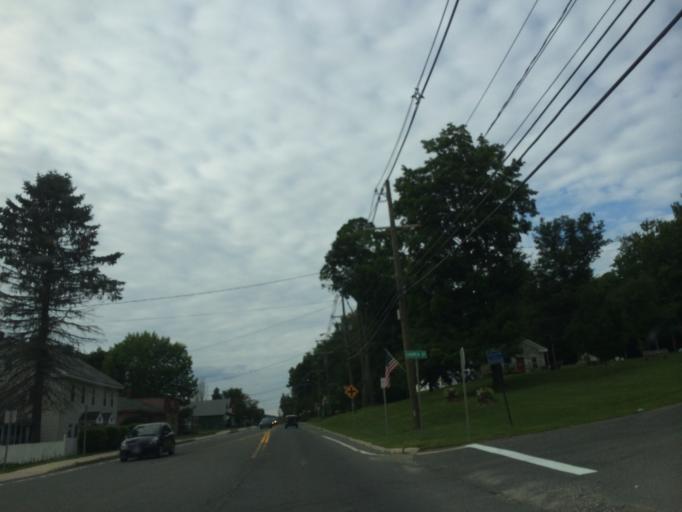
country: US
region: Massachusetts
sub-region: Berkshire County
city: Lanesborough
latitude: 42.5184
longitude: -73.2278
